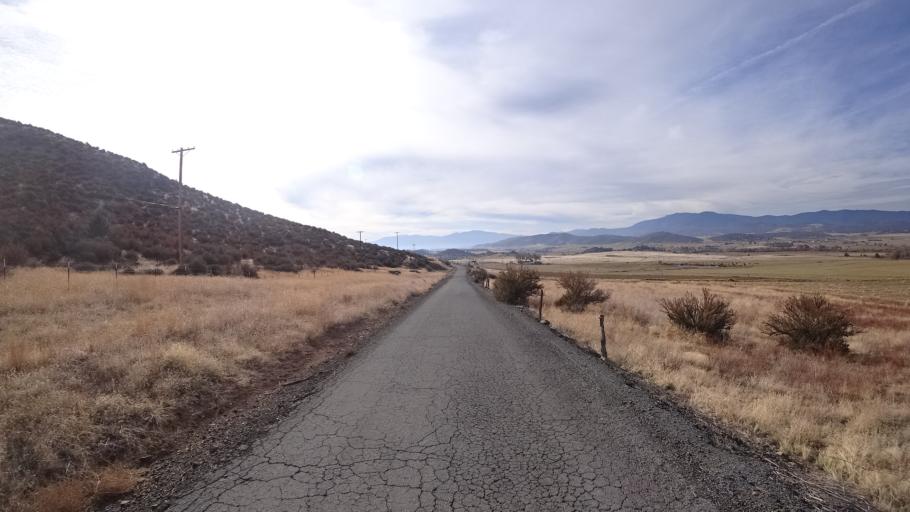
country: US
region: California
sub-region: Siskiyou County
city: Montague
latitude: 41.7143
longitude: -122.5216
